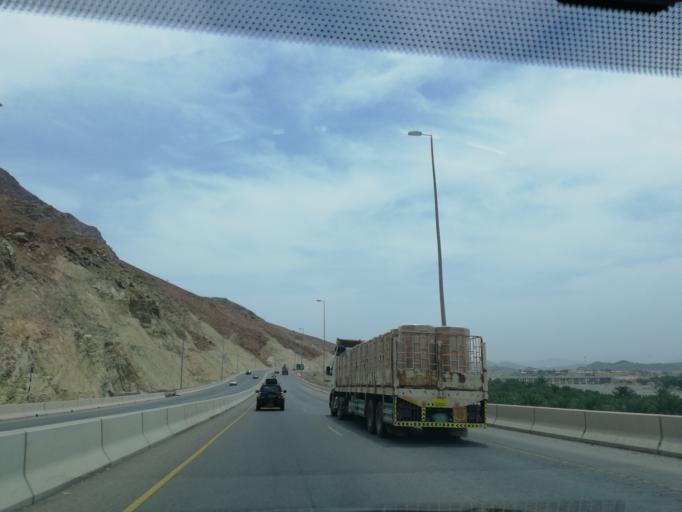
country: OM
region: Muhafazat ad Dakhiliyah
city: Bidbid
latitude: 23.4539
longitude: 58.1185
